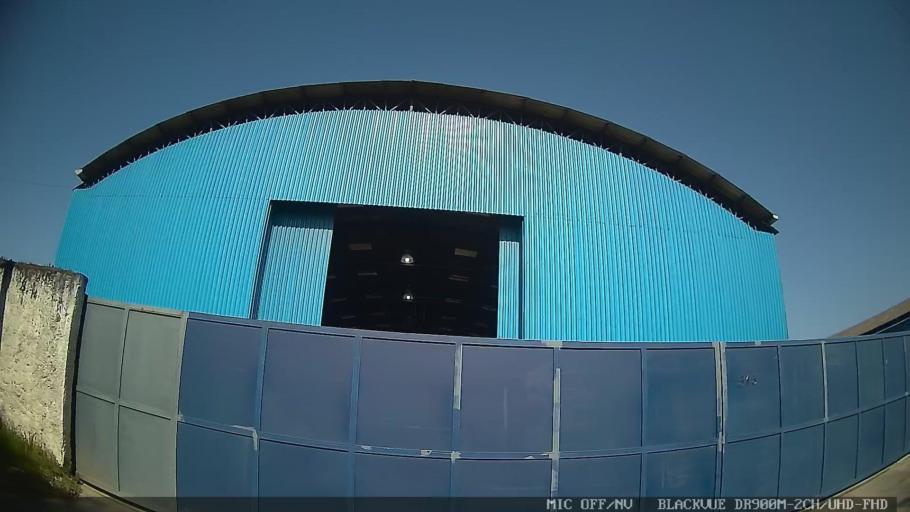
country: BR
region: Sao Paulo
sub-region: Guaruja
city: Guaruja
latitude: -24.0014
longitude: -46.2907
